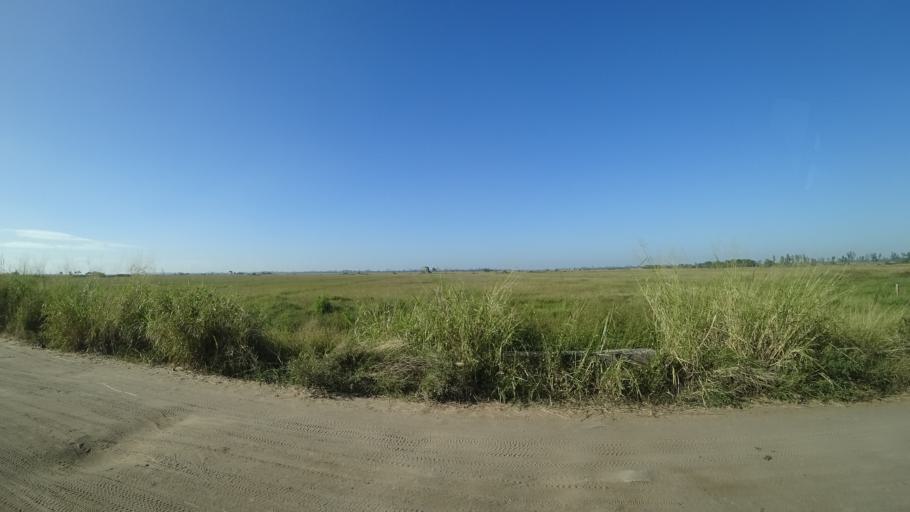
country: MZ
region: Sofala
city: Beira
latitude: -19.7632
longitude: 34.9042
